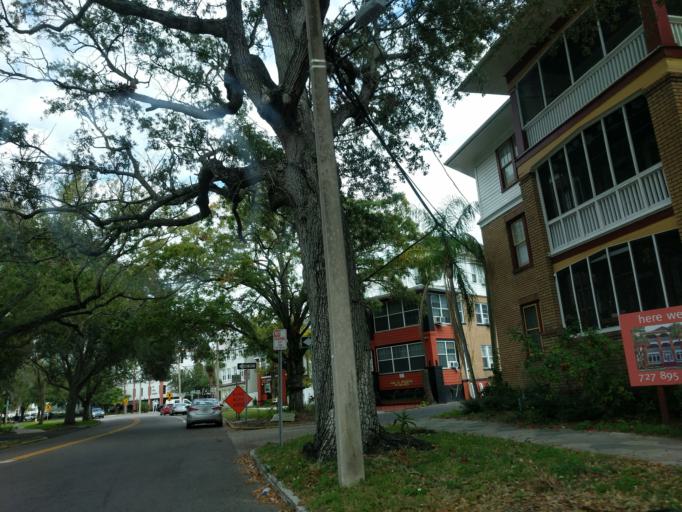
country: US
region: Florida
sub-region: Pinellas County
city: Saint Petersburg
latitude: 27.7741
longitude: -82.6402
